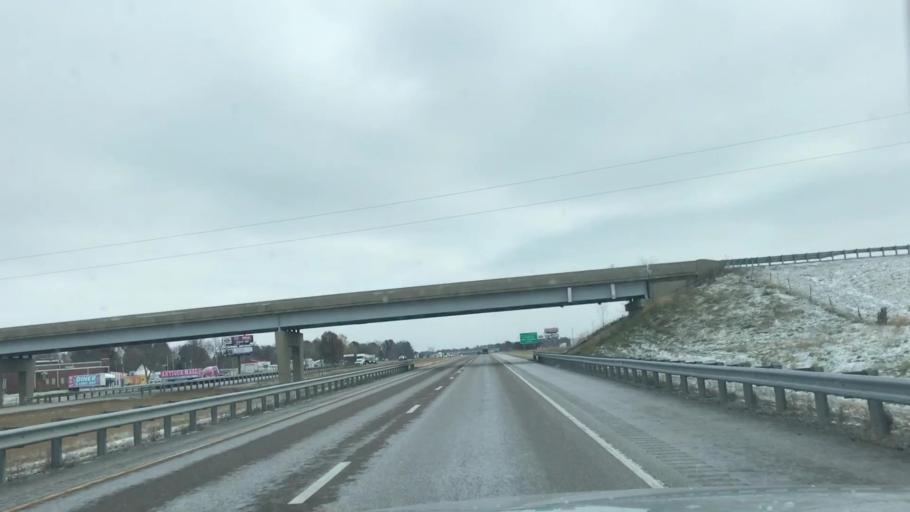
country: US
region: Illinois
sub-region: Macoupin County
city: Staunton
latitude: 38.9579
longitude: -89.7659
